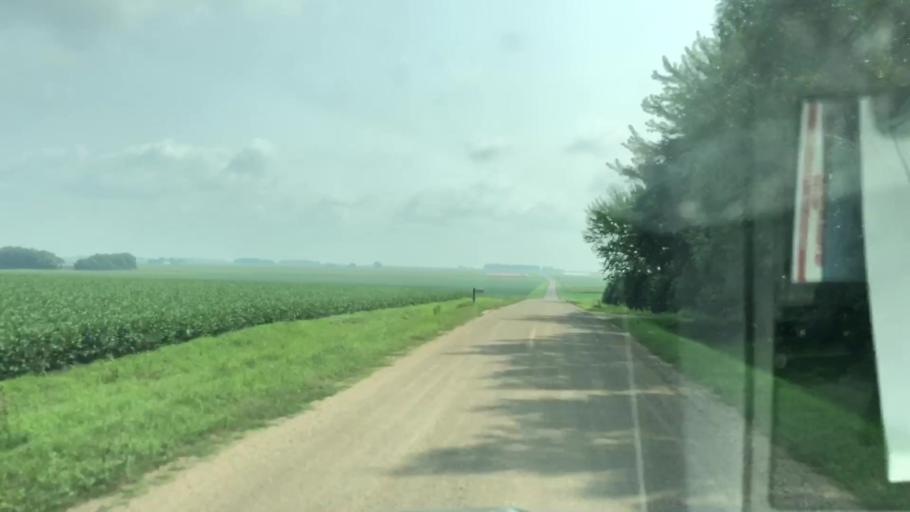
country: US
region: Iowa
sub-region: O'Brien County
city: Sheldon
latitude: 43.2152
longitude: -95.9355
